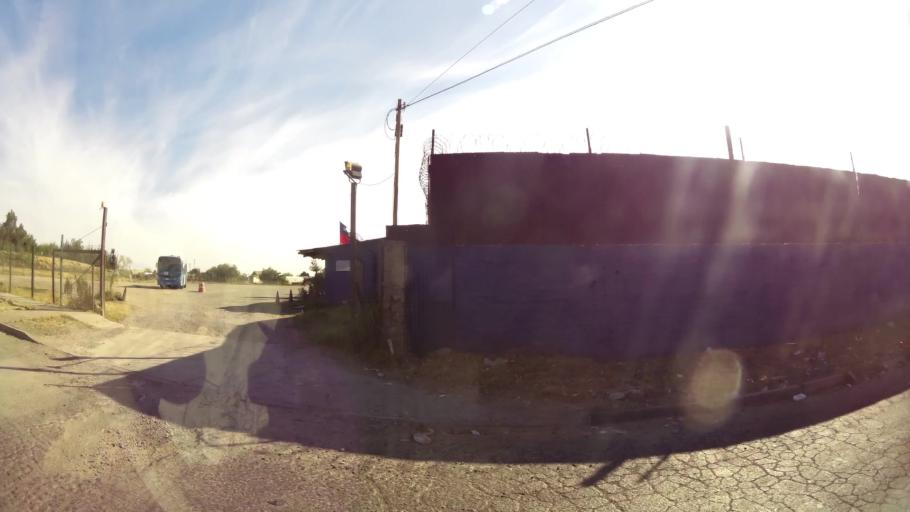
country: CL
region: Santiago Metropolitan
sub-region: Provincia de Santiago
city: Lo Prado
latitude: -33.4632
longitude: -70.6954
